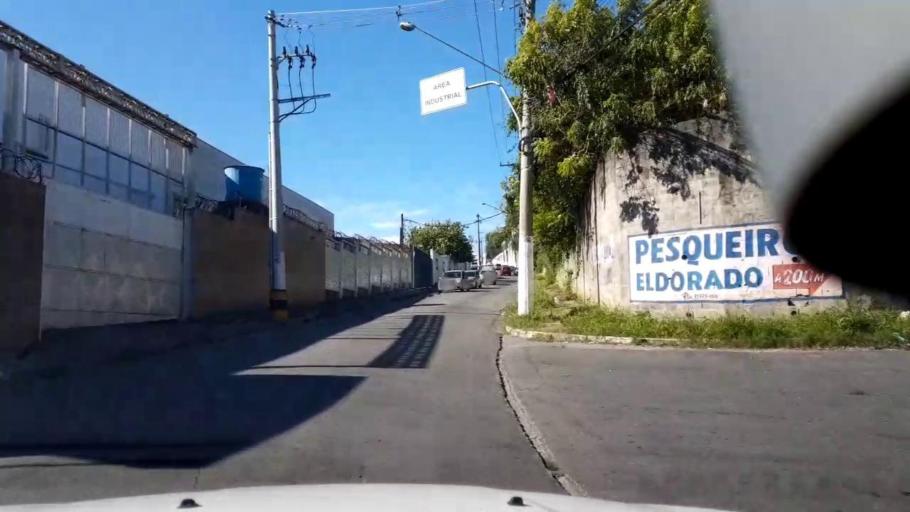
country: BR
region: Sao Paulo
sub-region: Ferraz De Vasconcelos
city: Ferraz de Vasconcelos
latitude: -23.5298
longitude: -46.3904
